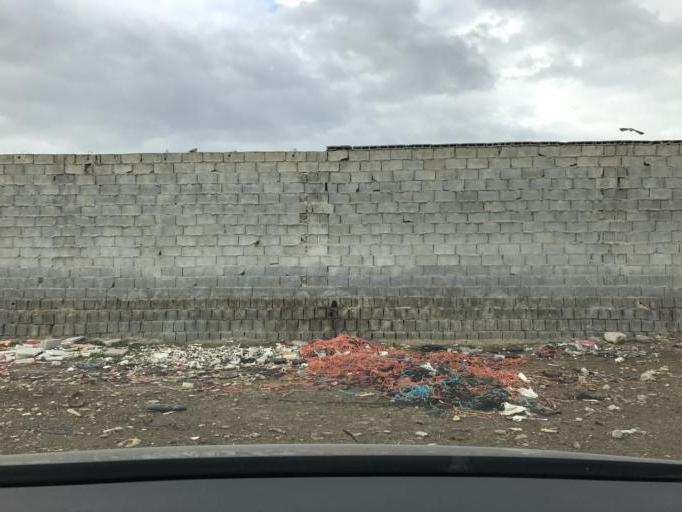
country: ES
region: Andalusia
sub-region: Provincia de Granada
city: Cullar-Vega
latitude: 37.1624
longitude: -3.6583
